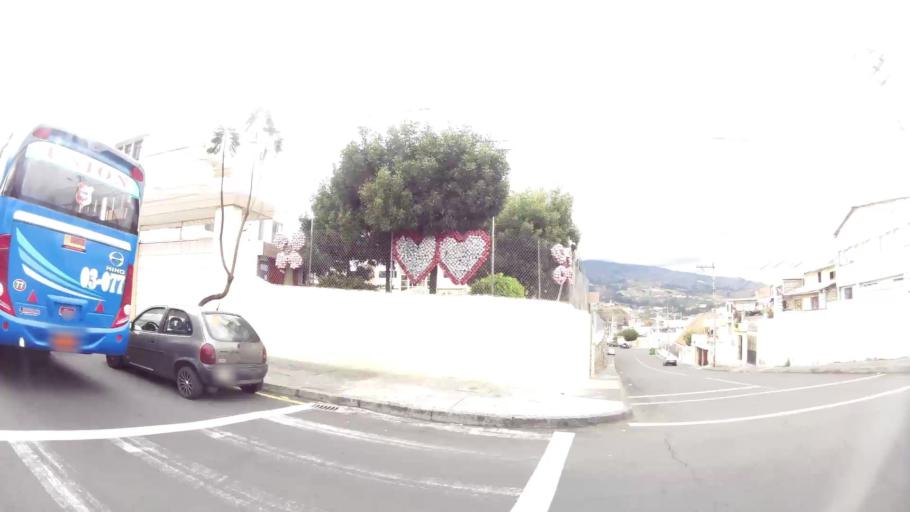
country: EC
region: Tungurahua
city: Ambato
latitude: -1.2504
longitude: -78.6341
